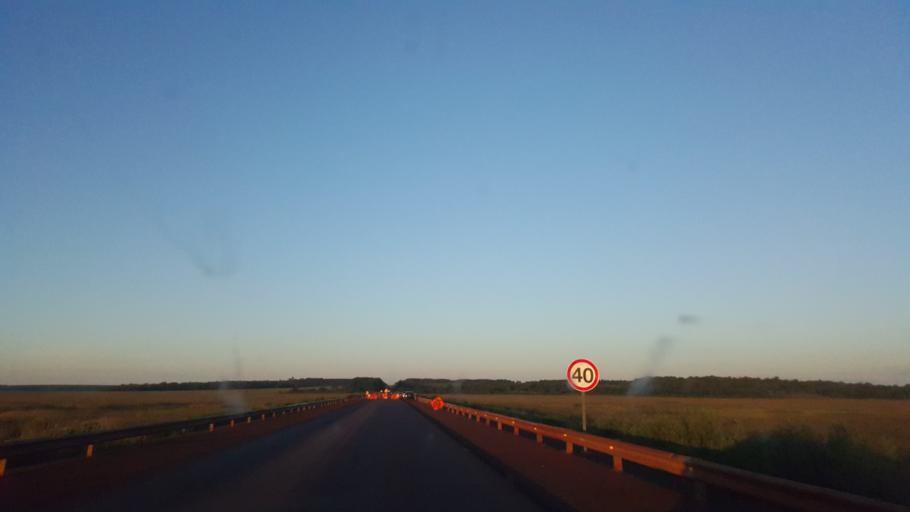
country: AR
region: Corrientes
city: Santo Tome
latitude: -28.3842
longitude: -55.9628
